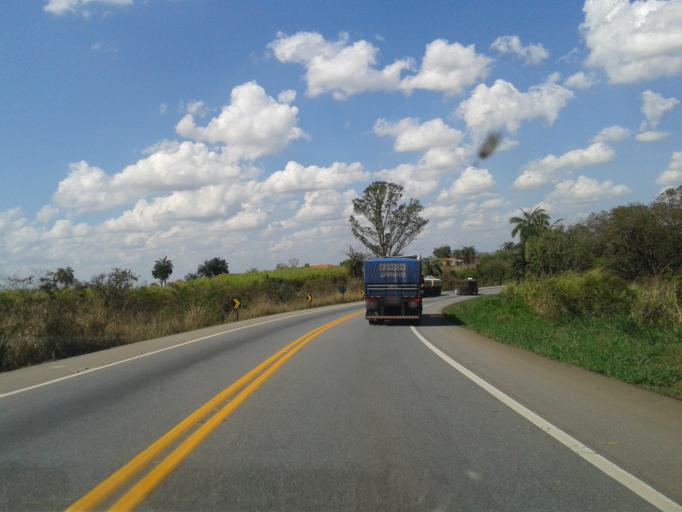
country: BR
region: Minas Gerais
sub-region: Luz
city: Luz
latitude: -19.7401
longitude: -45.8507
